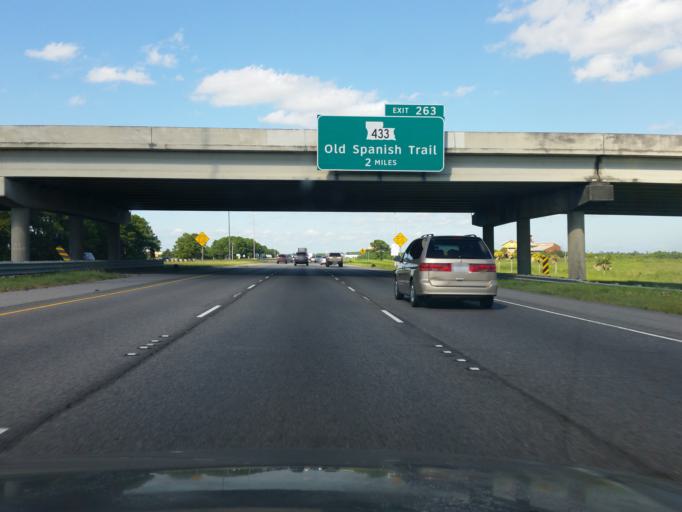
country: US
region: Louisiana
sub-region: Saint Tammany Parish
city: Eden Isle
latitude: 30.2217
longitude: -89.7834
